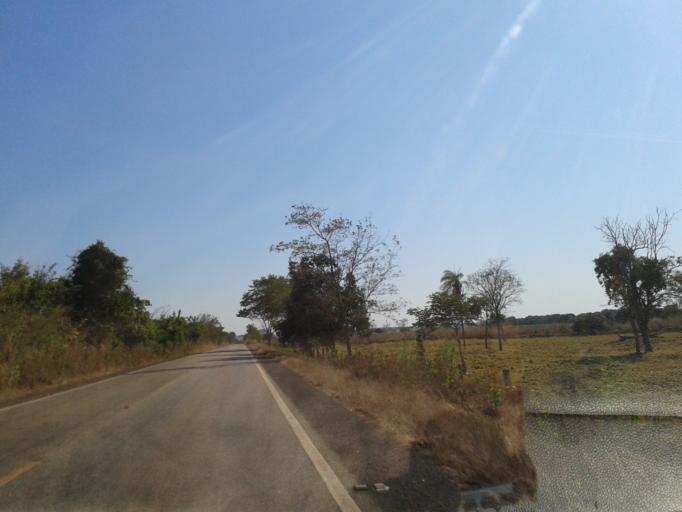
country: BR
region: Goias
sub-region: Mozarlandia
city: Mozarlandia
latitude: -14.6303
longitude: -50.5190
